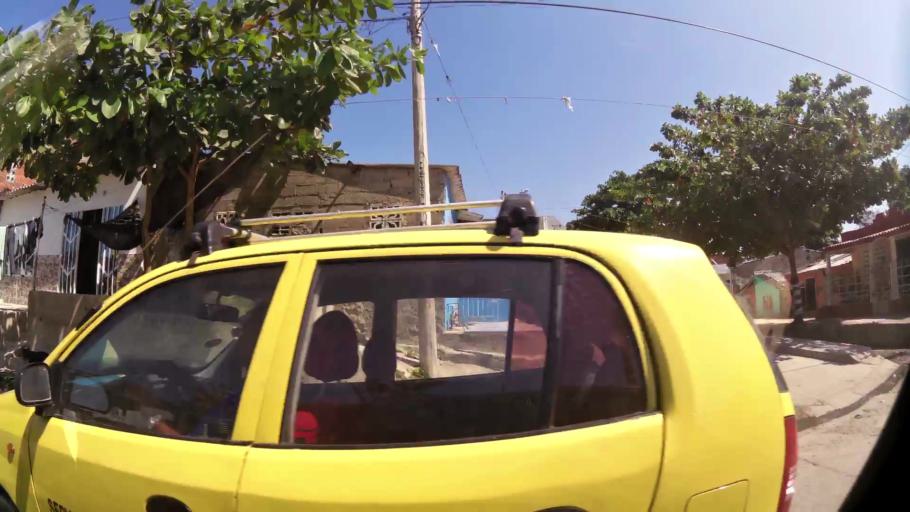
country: CO
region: Bolivar
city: Cartagena
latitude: 10.4348
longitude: -75.5175
